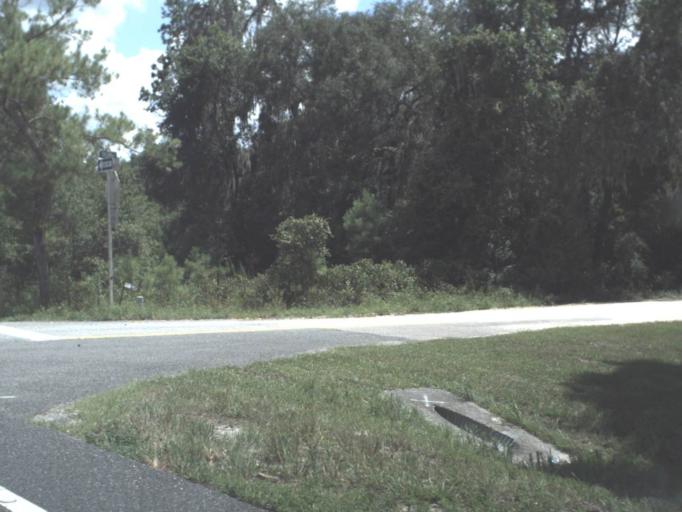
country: US
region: Florida
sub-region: Taylor County
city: Perry
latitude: 30.0296
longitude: -83.5408
